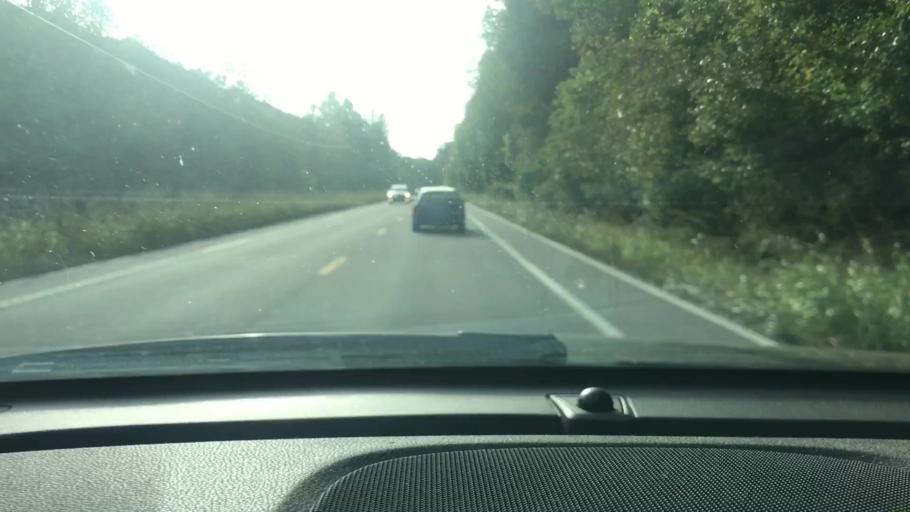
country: US
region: Tennessee
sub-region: Cheatham County
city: Pegram
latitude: 36.0155
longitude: -87.0366
